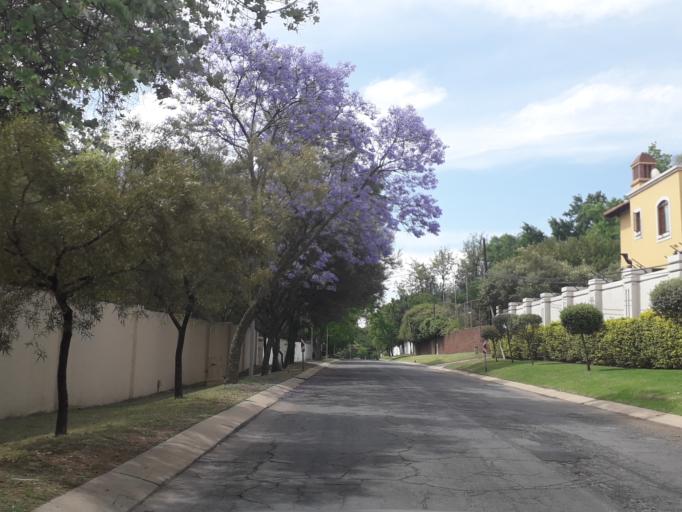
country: ZA
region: Gauteng
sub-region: City of Johannesburg Metropolitan Municipality
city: Diepsloot
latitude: -26.0624
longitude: 28.0175
